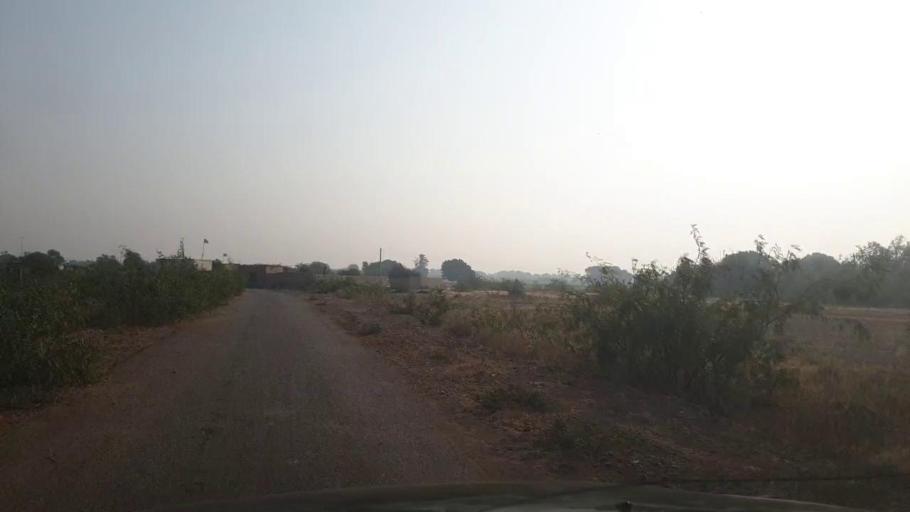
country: PK
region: Sindh
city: Kotri
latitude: 25.3151
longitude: 68.2382
